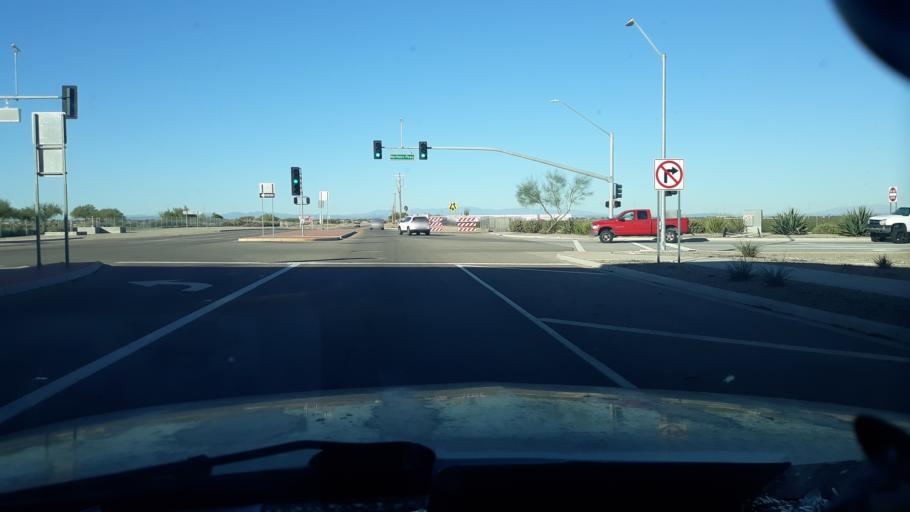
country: US
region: Arizona
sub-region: Maricopa County
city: Citrus Park
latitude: 33.5594
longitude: -112.3935
